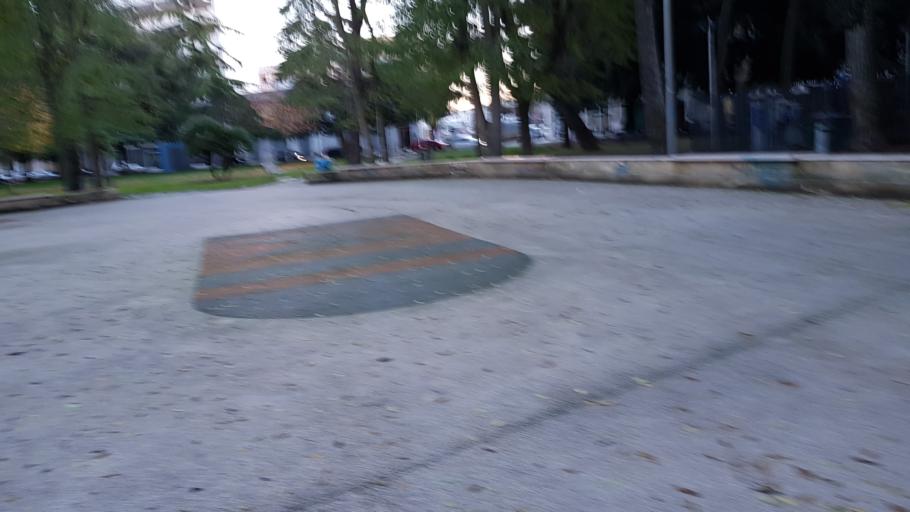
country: IT
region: Apulia
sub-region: Provincia di Bari
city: Gioia del Colle
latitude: 40.7957
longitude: 16.9224
